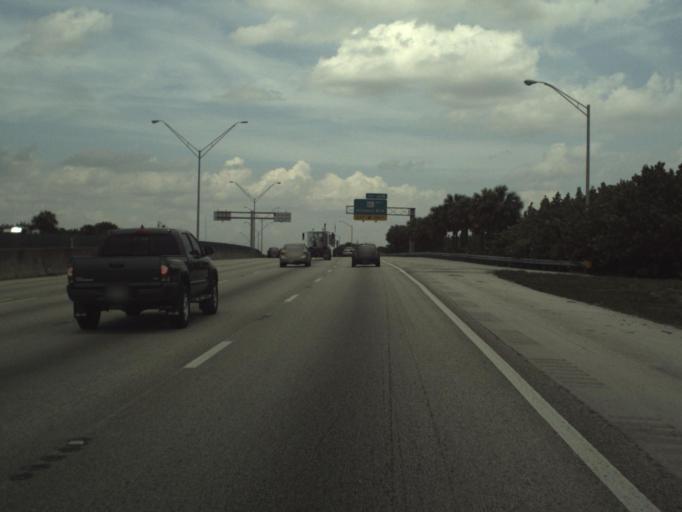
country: US
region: Florida
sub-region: Broward County
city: Deerfield Beach
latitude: 26.3160
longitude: -80.1163
